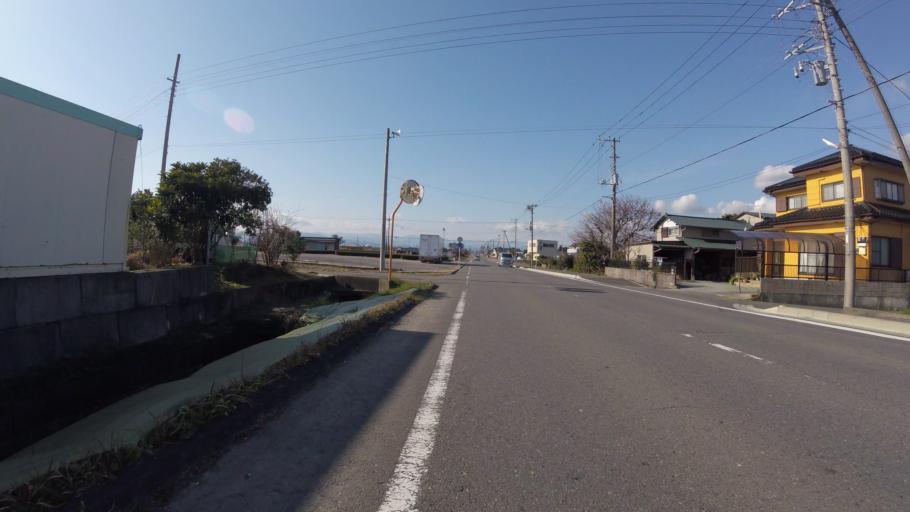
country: JP
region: Shizuoka
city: Fuji
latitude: 35.1477
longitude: 138.7722
